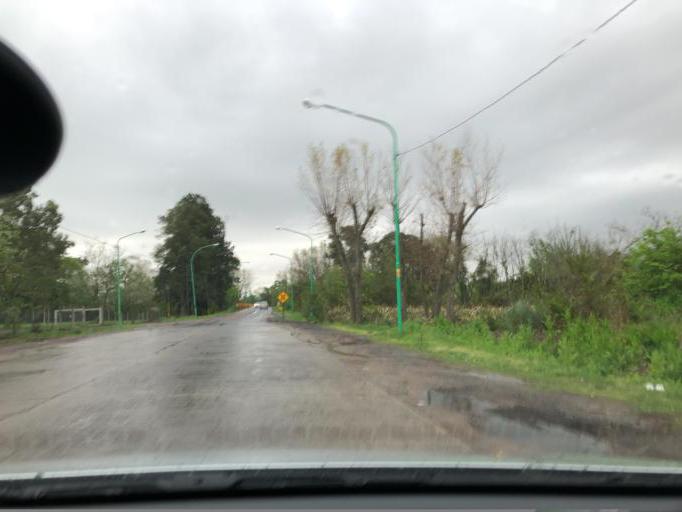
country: AR
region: Buenos Aires
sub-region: Partido de Ensenada
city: Ensenada
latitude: -34.8431
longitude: -57.9338
